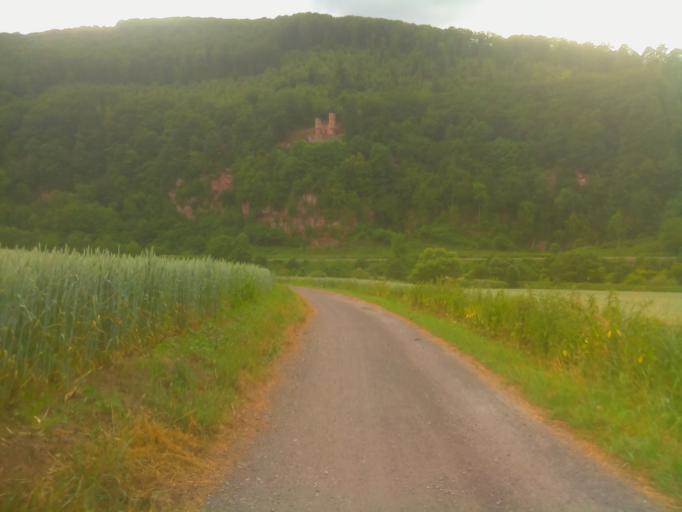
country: DE
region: Hesse
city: Neckarsteinach
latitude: 49.4064
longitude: 8.8306
